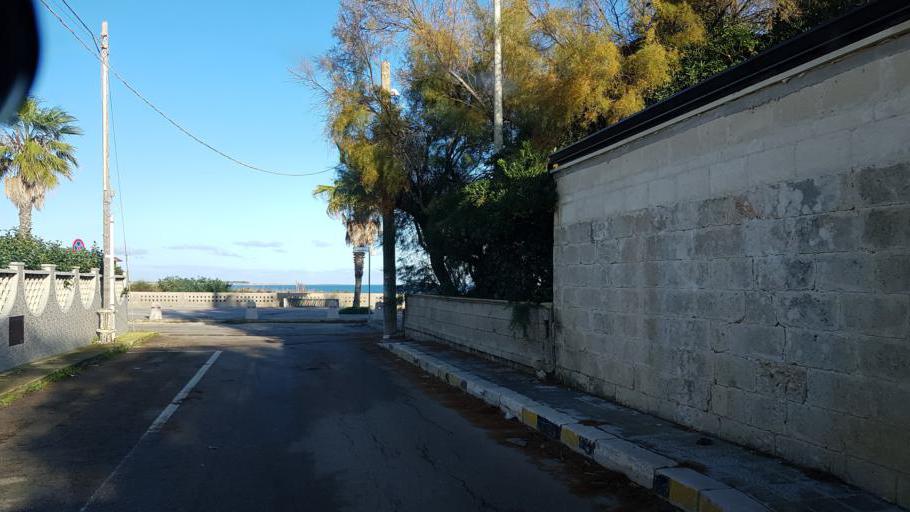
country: IT
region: Apulia
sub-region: Provincia di Brindisi
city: Torchiarolo
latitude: 40.5413
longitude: 18.0654
